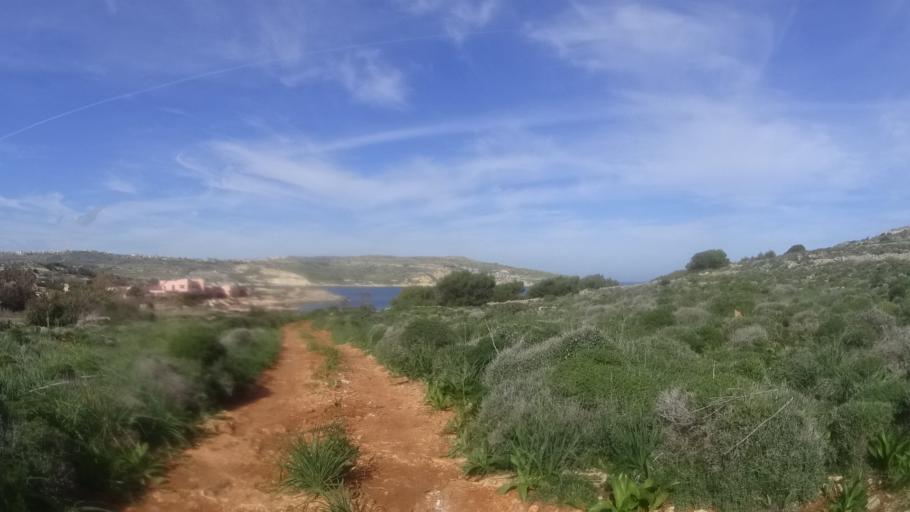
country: MT
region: Il-Qala
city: Qala
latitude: 36.0147
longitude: 14.3301
